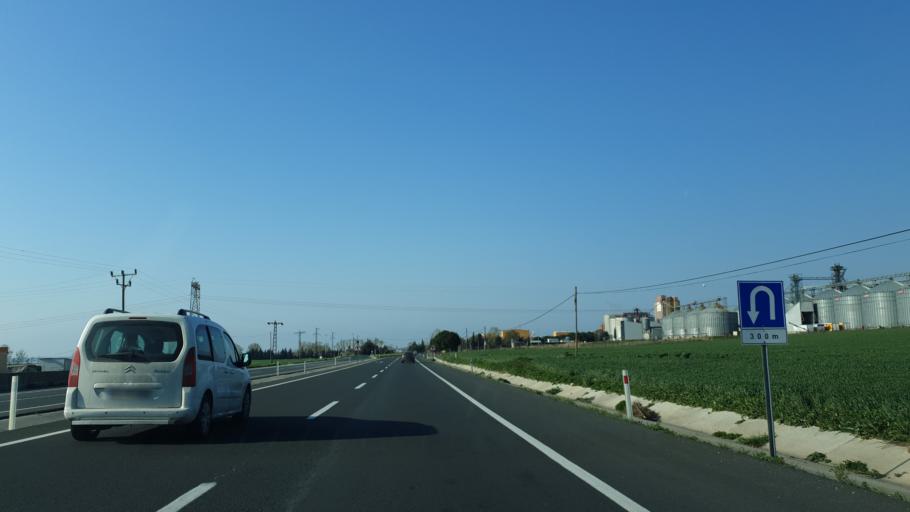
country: TR
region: Tekirdag
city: Corlu
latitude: 41.0267
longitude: 27.7249
